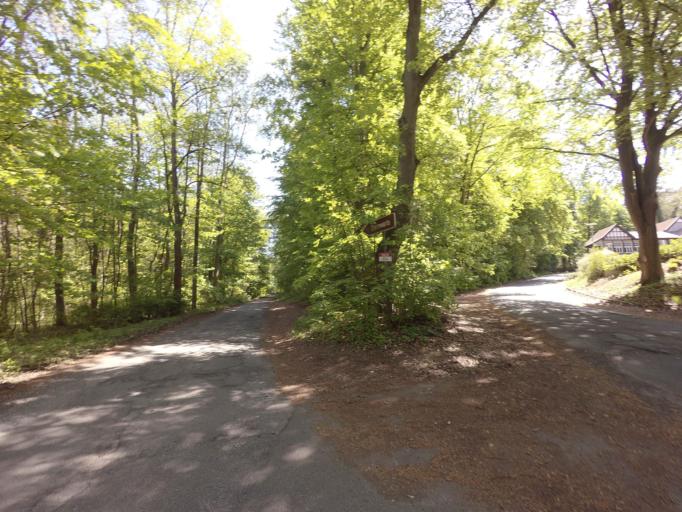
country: DE
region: Lower Saxony
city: Hildesheim
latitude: 52.1425
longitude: 9.9766
